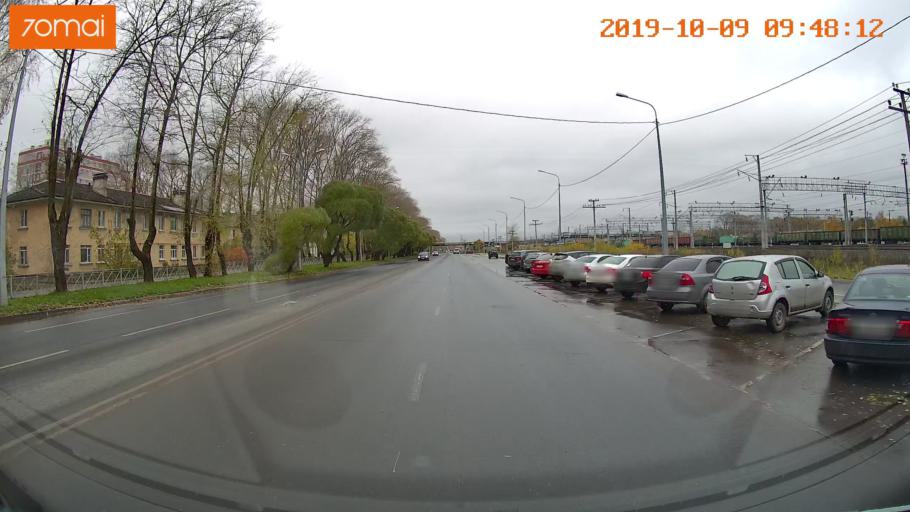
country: RU
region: Vologda
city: Vologda
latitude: 59.1935
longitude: 39.9324
